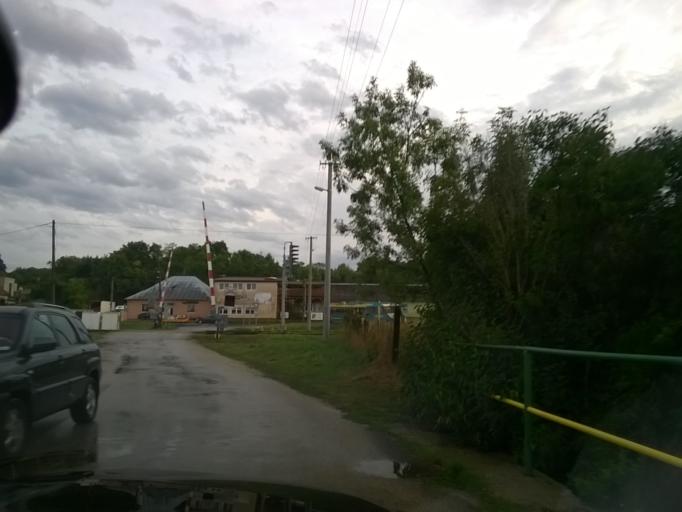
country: SK
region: Nitriansky
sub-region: Okres Nitra
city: Nitra
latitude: 48.3640
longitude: 17.9446
